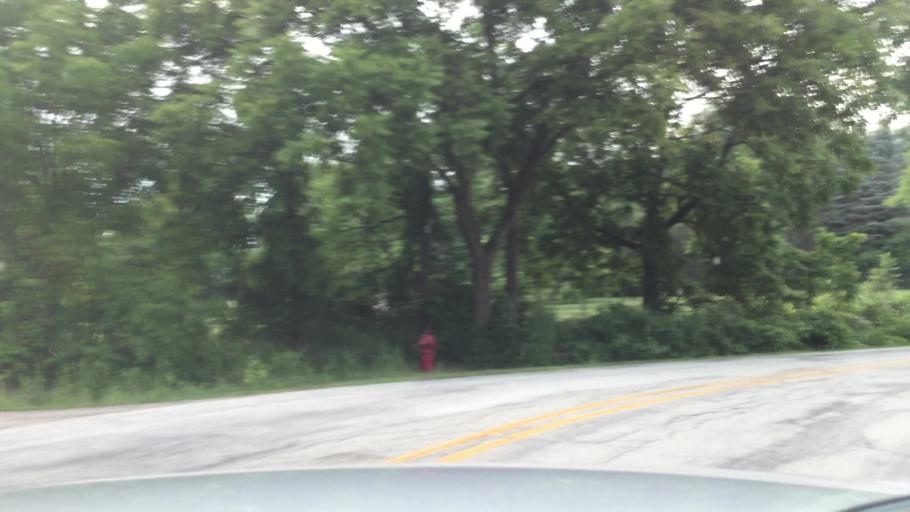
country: US
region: Michigan
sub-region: Saginaw County
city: Frankenmuth
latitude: 43.3323
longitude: -83.8095
